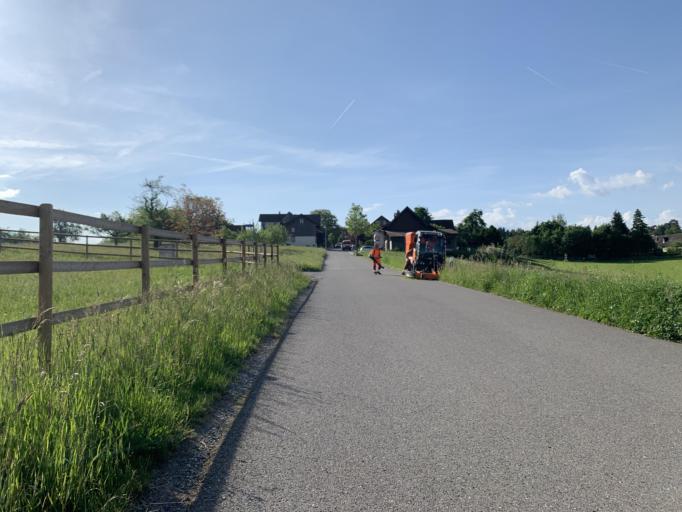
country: CH
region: Zurich
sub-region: Bezirk Hinwil
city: Wetzikon / Unter-Wetzikon
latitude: 47.2955
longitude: 8.8023
